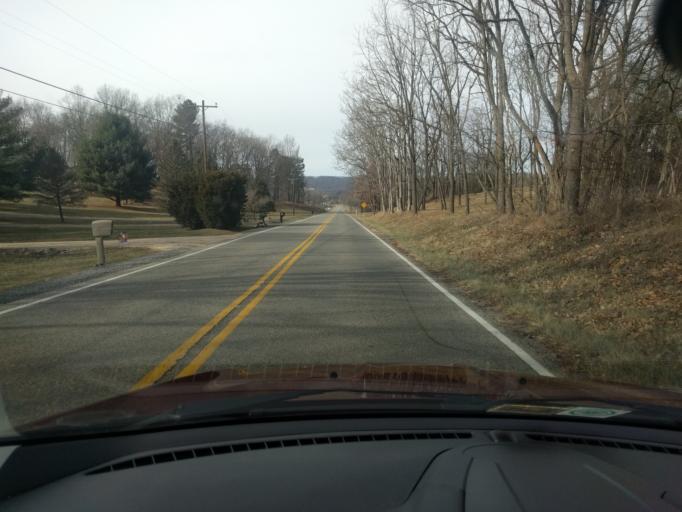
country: US
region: Virginia
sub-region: Augusta County
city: Stuarts Draft
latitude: 38.0377
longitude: -79.0753
